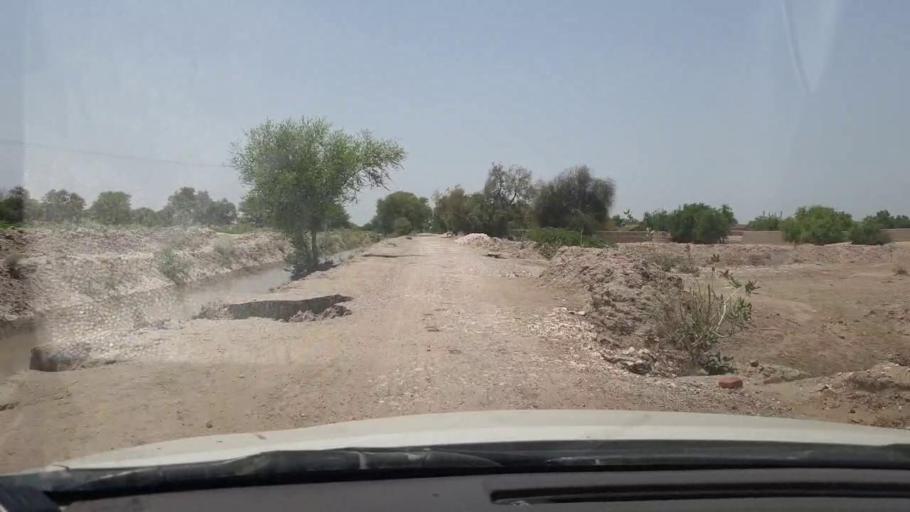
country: PK
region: Sindh
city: Rohri
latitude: 27.5158
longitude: 69.1842
